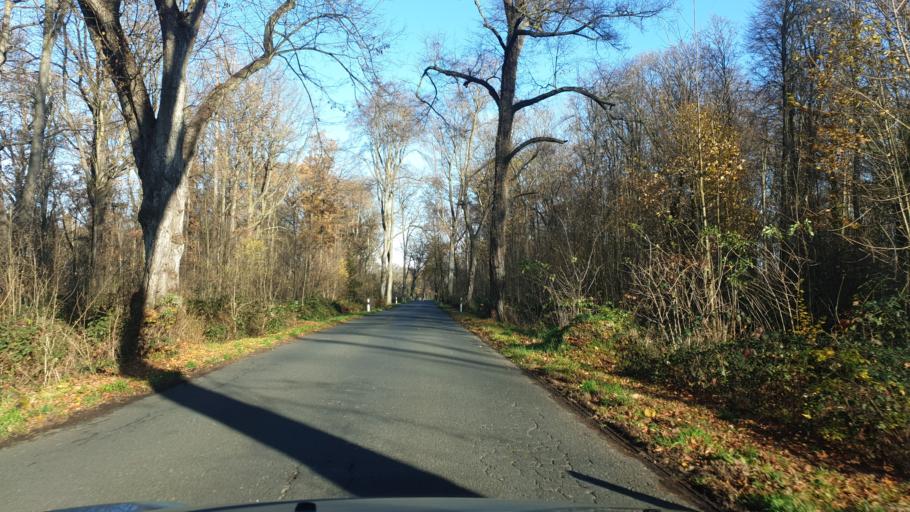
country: DE
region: Saxony-Anhalt
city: Droyssig
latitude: 51.0334
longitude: 12.0228
